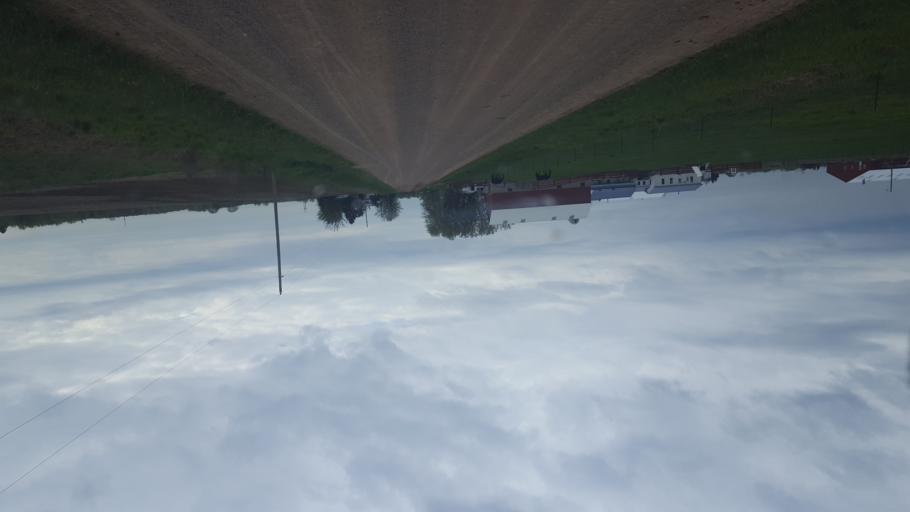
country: US
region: Wisconsin
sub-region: Marathon County
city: Spencer
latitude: 44.6483
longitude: -90.3772
